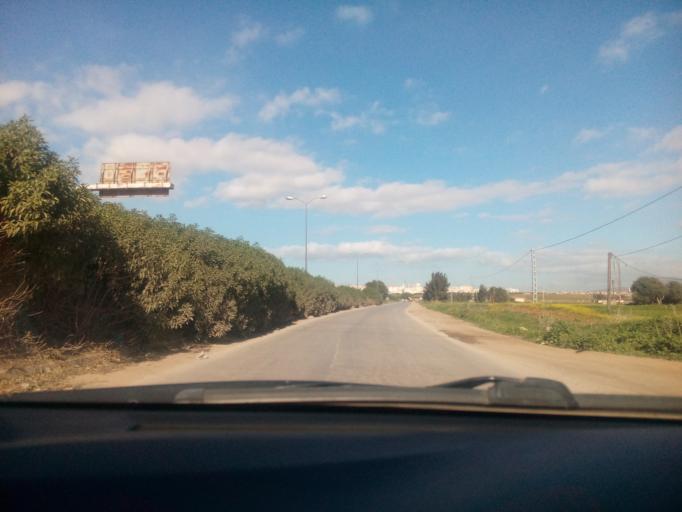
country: DZ
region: Oran
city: Sidi ech Chahmi
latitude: 35.6702
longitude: -0.5661
